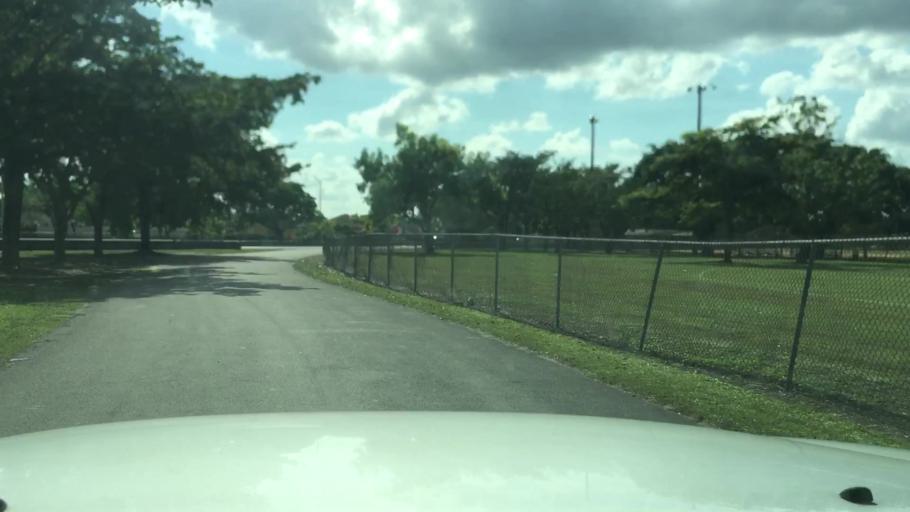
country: US
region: Florida
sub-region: Miami-Dade County
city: University Park
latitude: 25.7475
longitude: -80.3768
